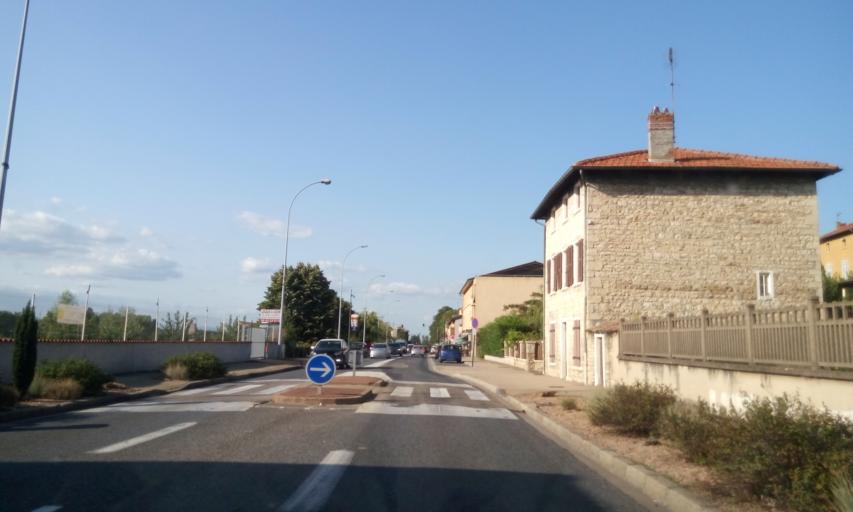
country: FR
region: Rhone-Alpes
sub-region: Departement du Rhone
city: Lissieu
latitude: 45.8631
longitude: 4.7425
